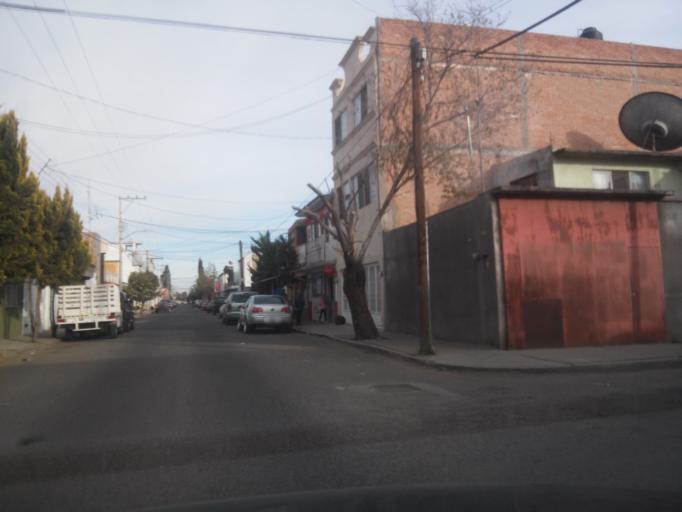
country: MX
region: Durango
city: Victoria de Durango
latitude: 24.0242
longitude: -104.6430
